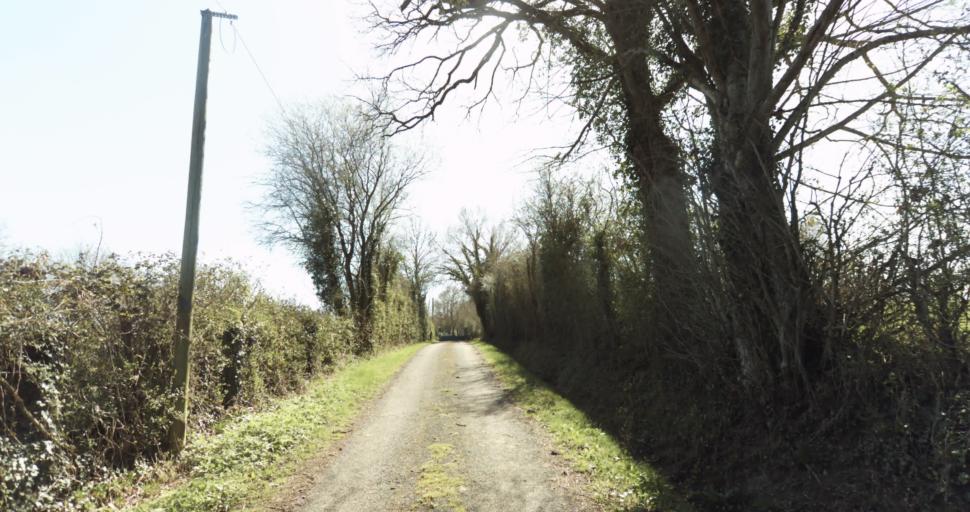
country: FR
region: Lower Normandy
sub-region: Departement du Calvados
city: Saint-Pierre-sur-Dives
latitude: 48.9584
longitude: 0.0005
